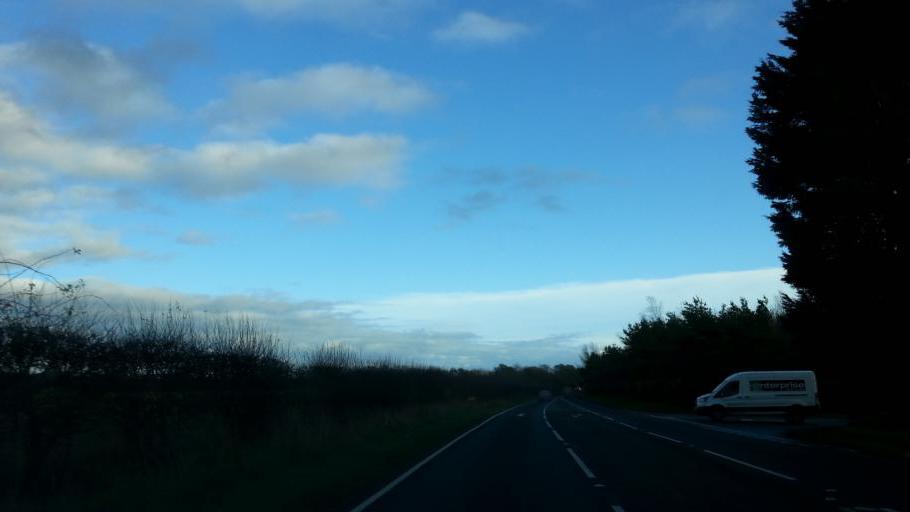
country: GB
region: England
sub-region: Oxfordshire
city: Shrivenham
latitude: 51.6159
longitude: -1.6287
